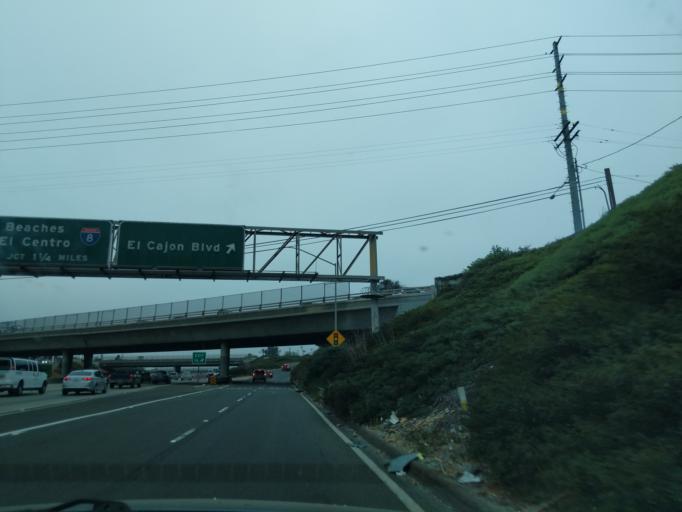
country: US
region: California
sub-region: San Diego County
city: San Diego
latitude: 32.7528
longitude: -117.1238
